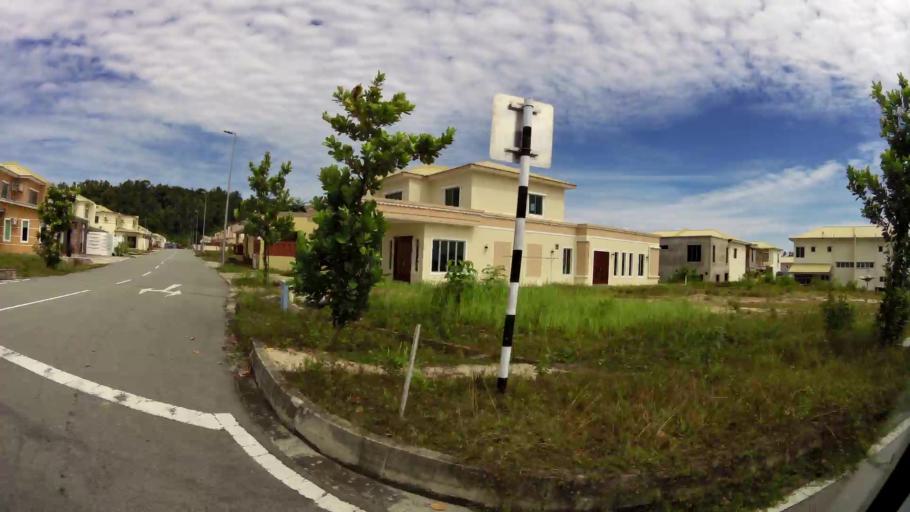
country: BN
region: Brunei and Muara
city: Bandar Seri Begawan
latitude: 4.9833
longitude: 115.0122
